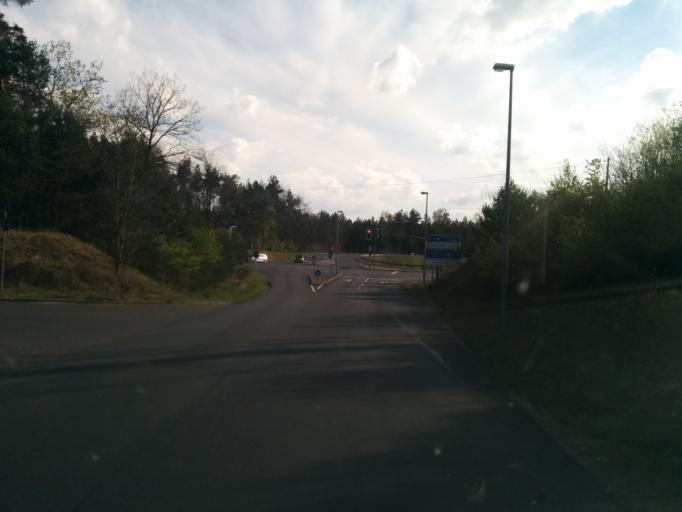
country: DE
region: Brandenburg
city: Stahnsdorf
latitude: 52.4026
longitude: 13.1890
